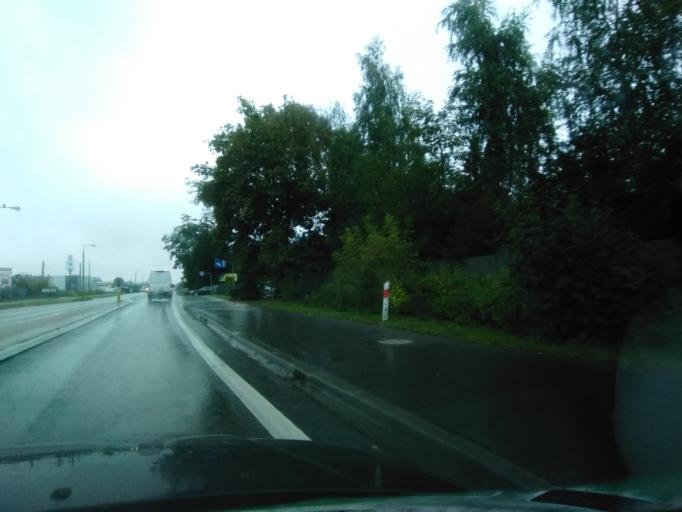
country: PL
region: Subcarpathian Voivodeship
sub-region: Powiat debicki
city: Debica
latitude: 50.0571
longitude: 21.4451
